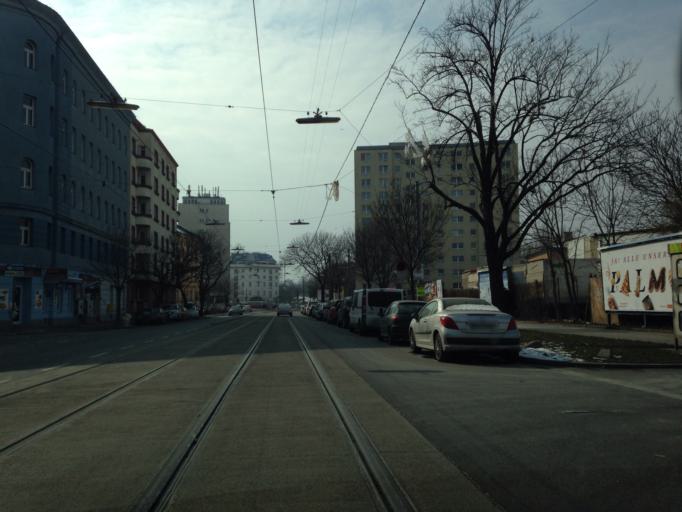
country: AT
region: Vienna
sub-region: Wien Stadt
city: Vienna
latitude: 48.2269
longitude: 16.3863
